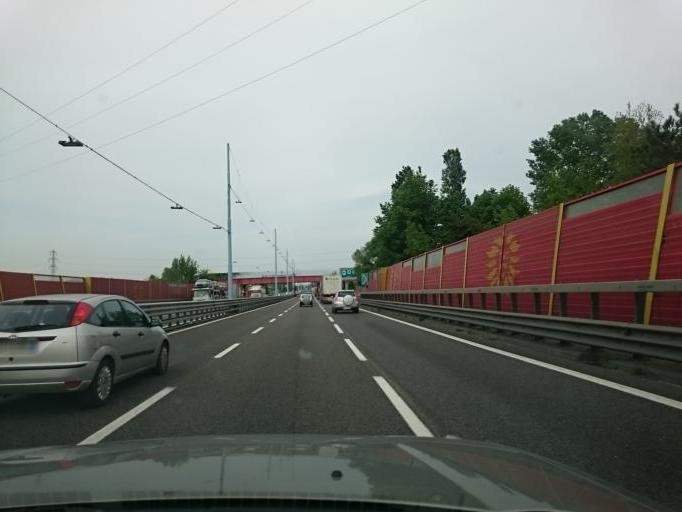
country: IT
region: Veneto
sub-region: Provincia di Treviso
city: Mogliano Veneto
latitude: 45.5219
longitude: 12.2553
